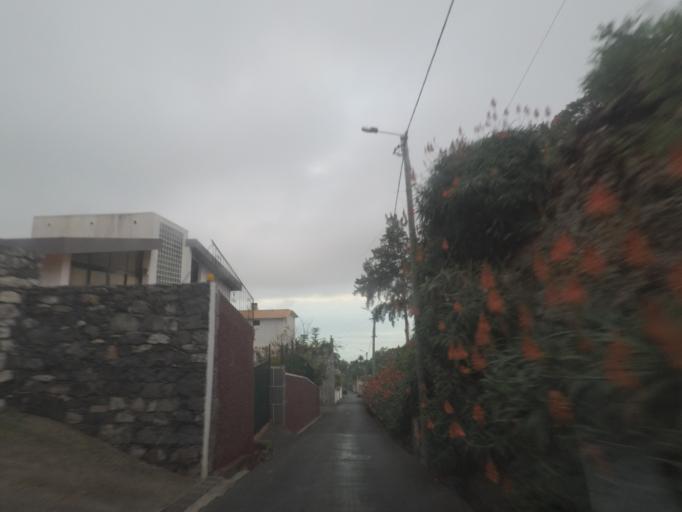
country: PT
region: Madeira
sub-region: Funchal
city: Nossa Senhora do Monte
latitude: 32.6703
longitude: -16.9043
